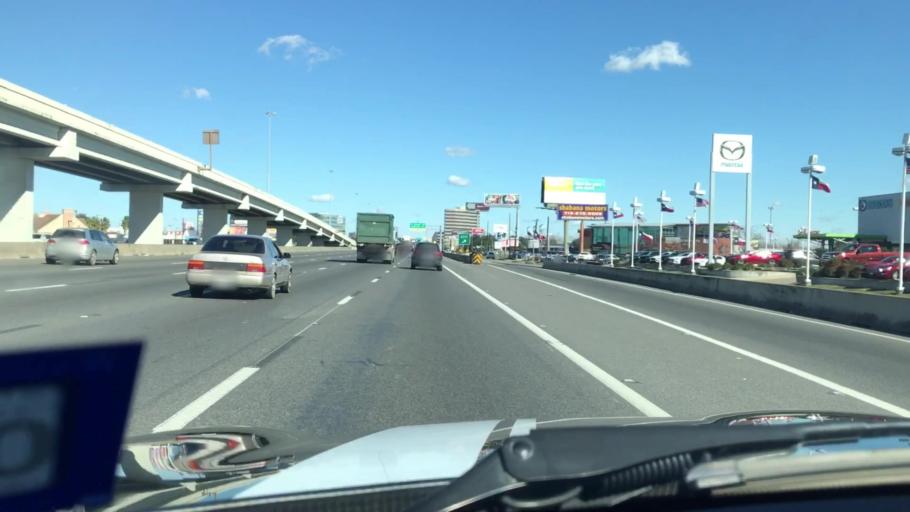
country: US
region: Texas
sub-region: Fort Bend County
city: Meadows Place
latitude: 29.6718
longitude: -95.5461
